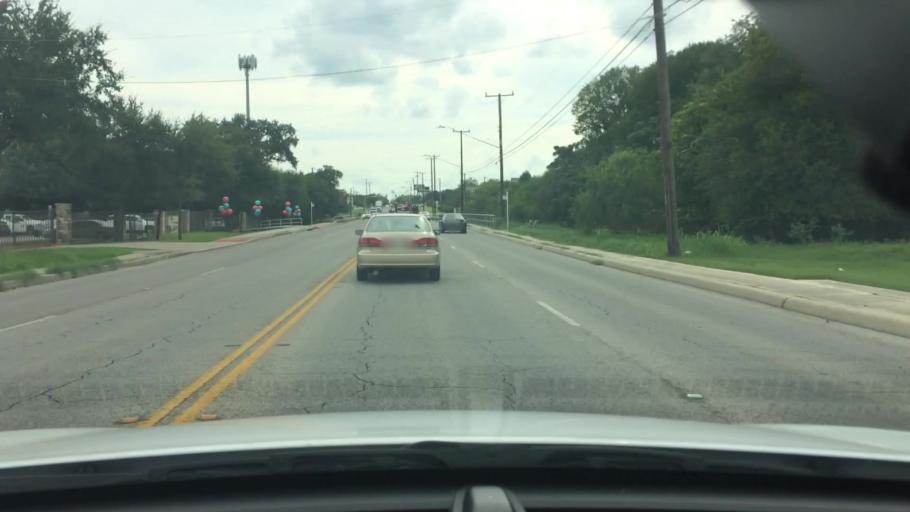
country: US
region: Texas
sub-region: Bexar County
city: Leon Valley
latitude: 29.5156
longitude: -98.6080
